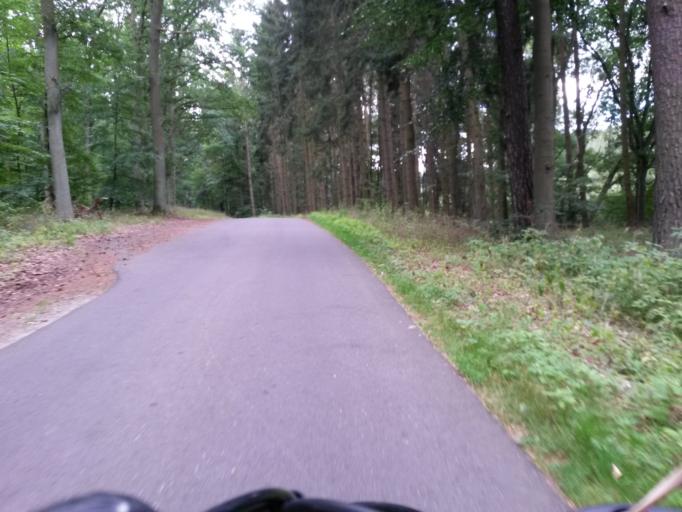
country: DE
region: Brandenburg
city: Angermunde
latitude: 53.0622
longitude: 13.9336
